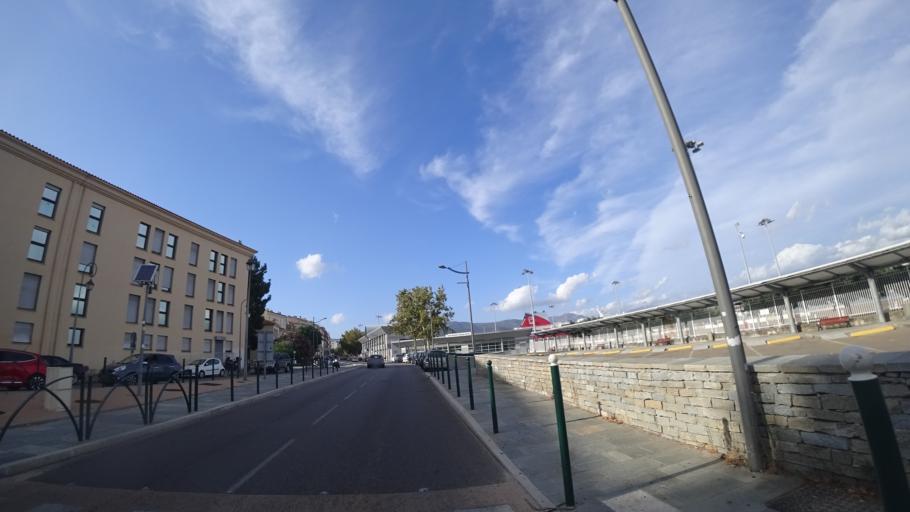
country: FR
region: Corsica
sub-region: Departement de la Corse-du-Sud
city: Ajaccio
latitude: 41.9220
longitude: 8.7396
